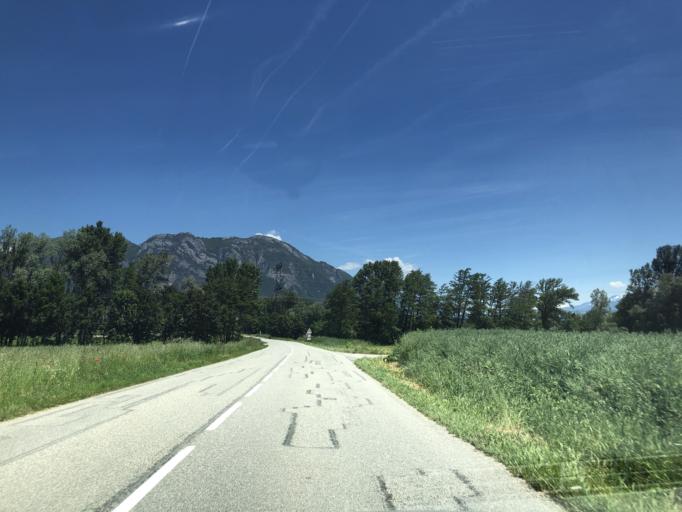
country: FR
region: Rhone-Alpes
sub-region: Departement de l'Isere
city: Chapareillan
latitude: 45.4725
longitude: 6.0070
